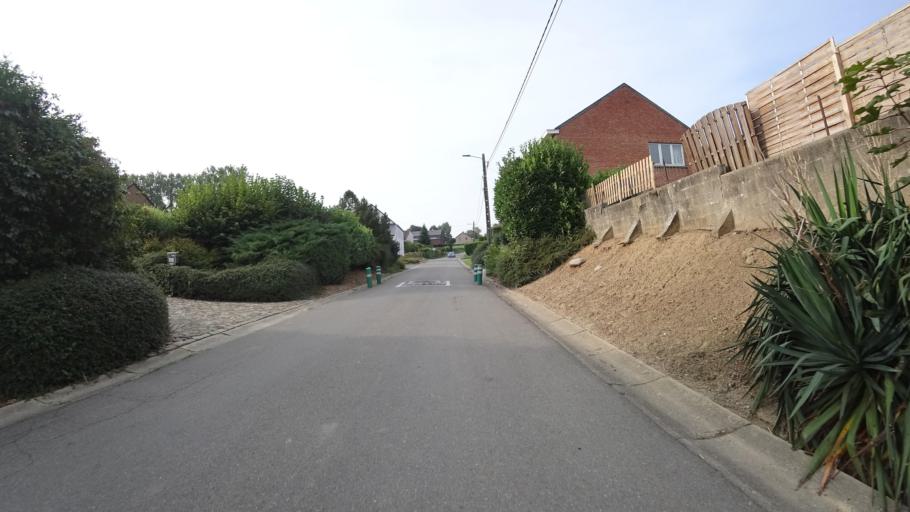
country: BE
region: Wallonia
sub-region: Province de Namur
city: Namur
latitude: 50.5170
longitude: 4.8397
